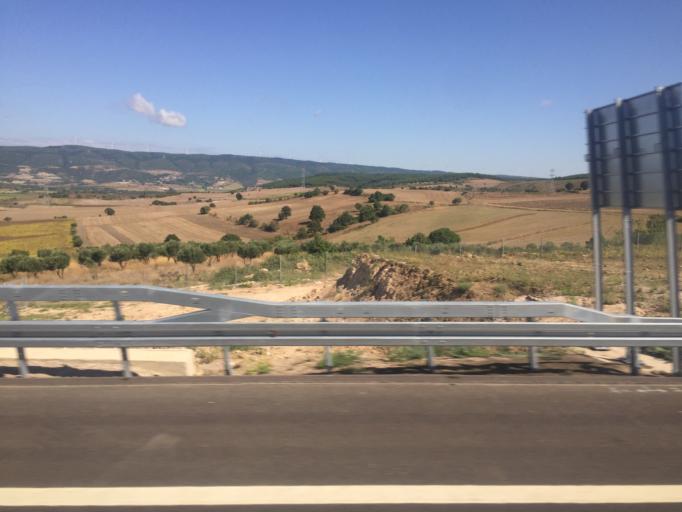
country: TR
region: Bursa
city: Mahmudiye
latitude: 40.2767
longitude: 28.5246
